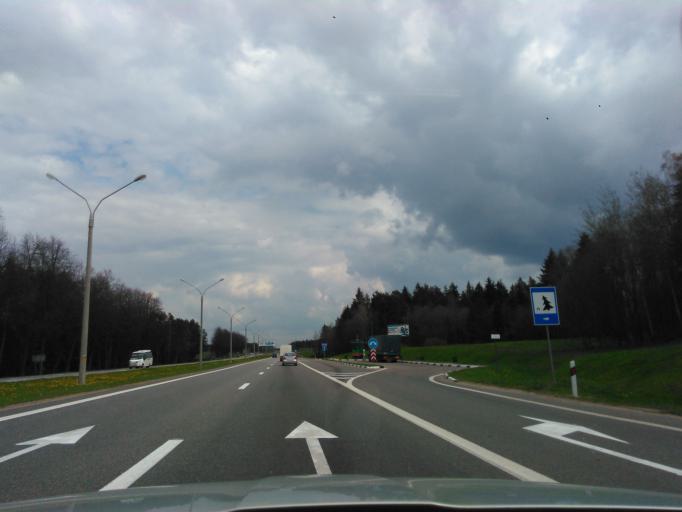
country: BY
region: Minsk
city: Korolev Stan
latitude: 53.9934
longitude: 27.8119
